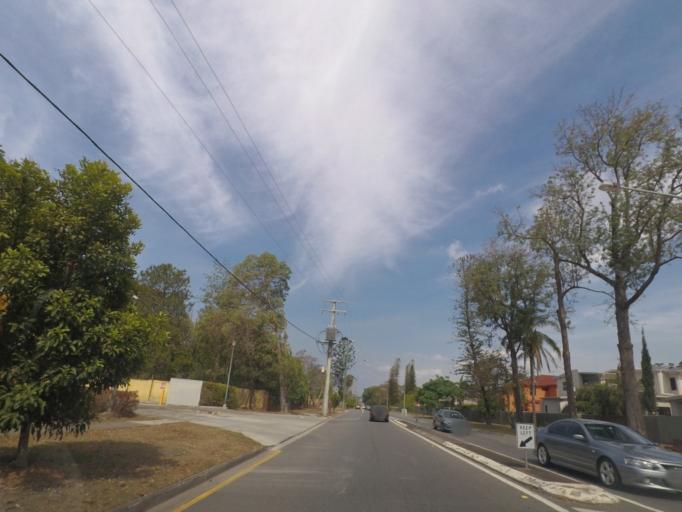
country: AU
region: Queensland
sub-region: Brisbane
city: Sunnybank
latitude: -27.5974
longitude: 153.0446
